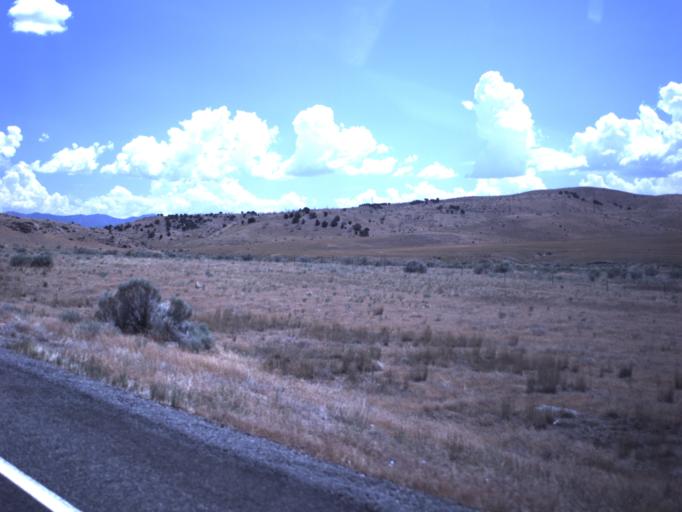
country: US
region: Utah
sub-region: Juab County
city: Nephi
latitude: 39.6388
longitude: -112.0937
